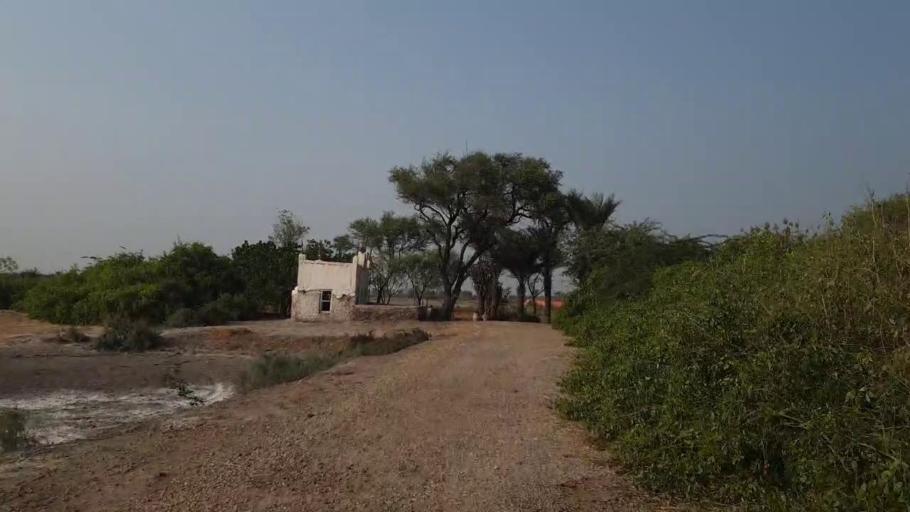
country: PK
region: Sindh
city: Tando Muhammad Khan
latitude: 25.0810
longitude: 68.3393
